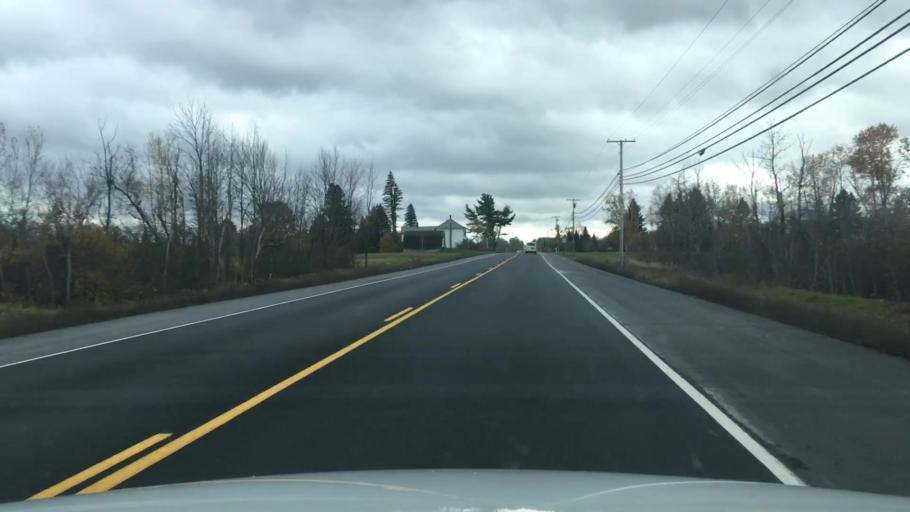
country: US
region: Maine
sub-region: Aroostook County
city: Houlton
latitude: 46.2502
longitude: -67.8408
